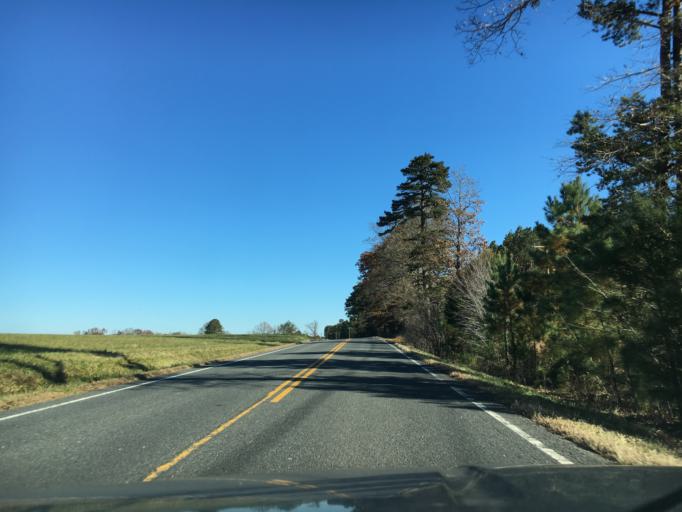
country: US
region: Virginia
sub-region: Buckingham County
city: Buckingham
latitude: 37.4903
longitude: -78.6373
